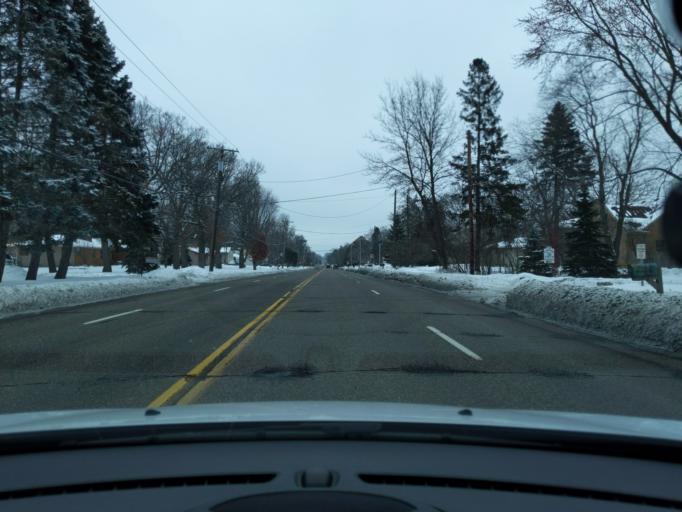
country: US
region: Minnesota
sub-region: Ramsey County
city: Roseville
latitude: 45.0207
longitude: -93.1319
